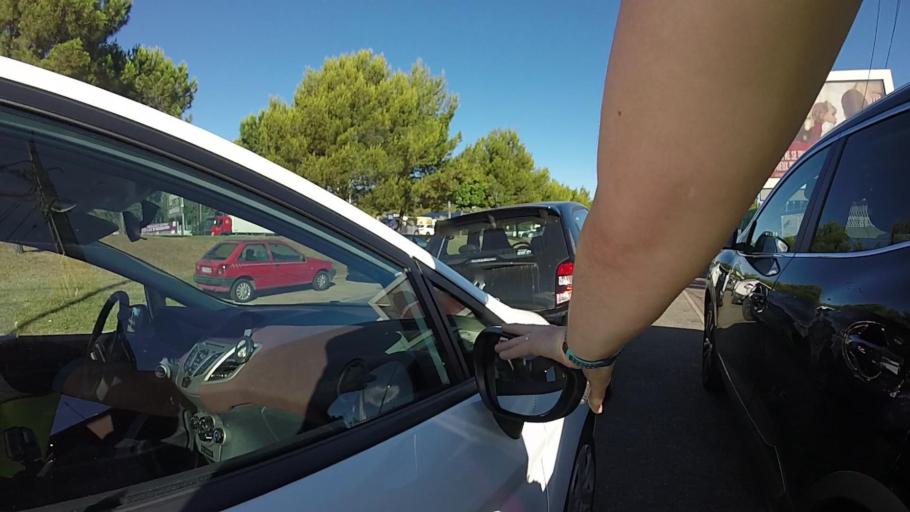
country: FR
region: Provence-Alpes-Cote d'Azur
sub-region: Departement des Alpes-Maritimes
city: Biot
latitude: 43.5976
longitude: 7.0894
